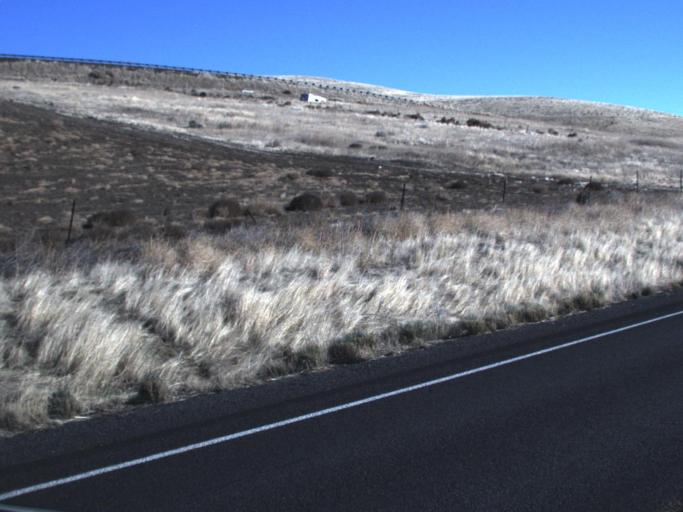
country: US
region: Washington
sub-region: Garfield County
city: Pomeroy
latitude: 46.4760
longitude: -117.6543
